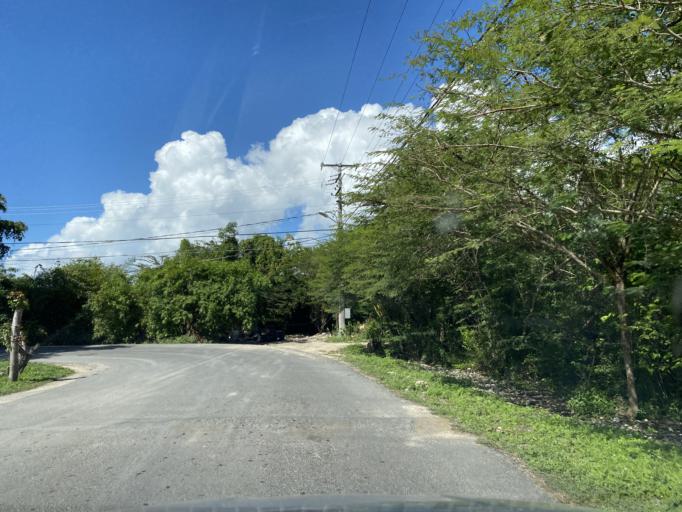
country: DO
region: La Romana
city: La Romana
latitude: 18.3509
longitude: -68.8295
